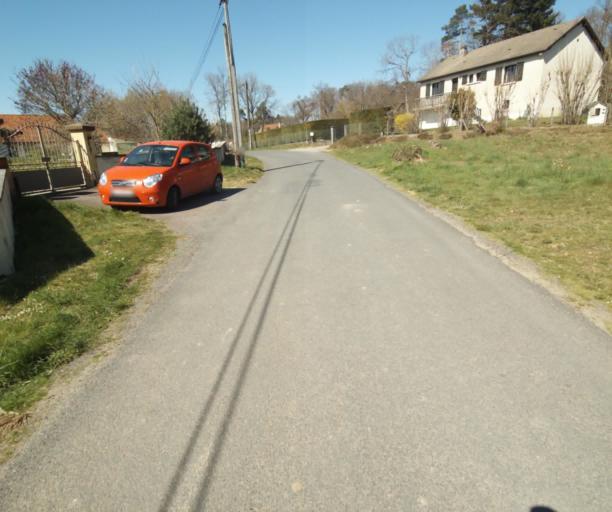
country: FR
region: Limousin
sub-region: Departement de la Correze
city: Saint-Mexant
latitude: 45.2849
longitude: 1.6438
